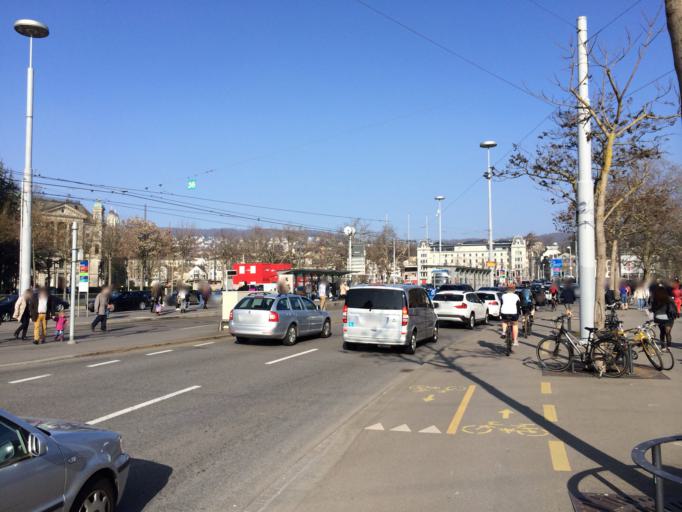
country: CH
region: Zurich
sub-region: Bezirk Zuerich
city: Zuerich (Kreis 1)
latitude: 47.3663
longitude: 8.5407
